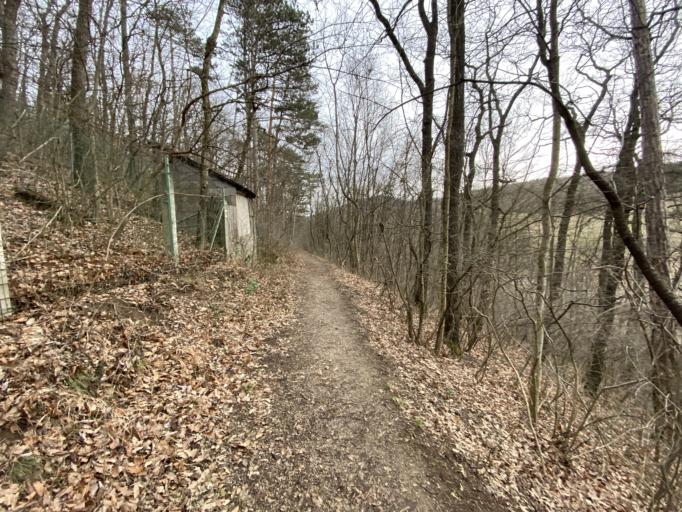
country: AT
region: Lower Austria
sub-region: Politischer Bezirk Modling
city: Gaaden
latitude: 48.0332
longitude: 16.1773
